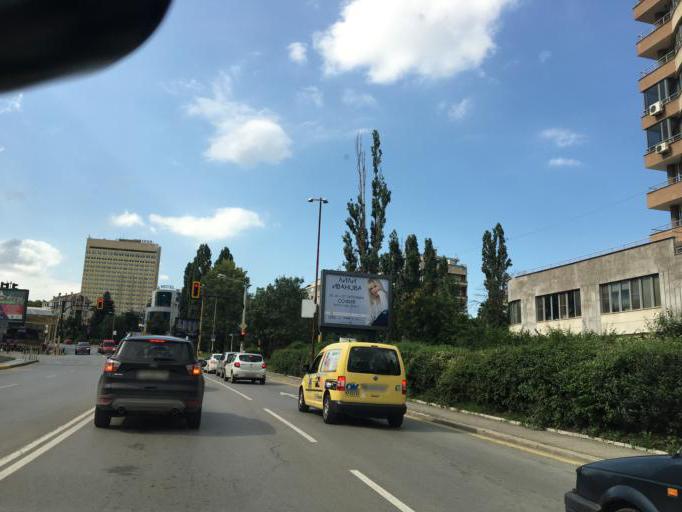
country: BG
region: Sofia-Capital
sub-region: Stolichna Obshtina
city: Sofia
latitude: 42.6707
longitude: 23.3518
